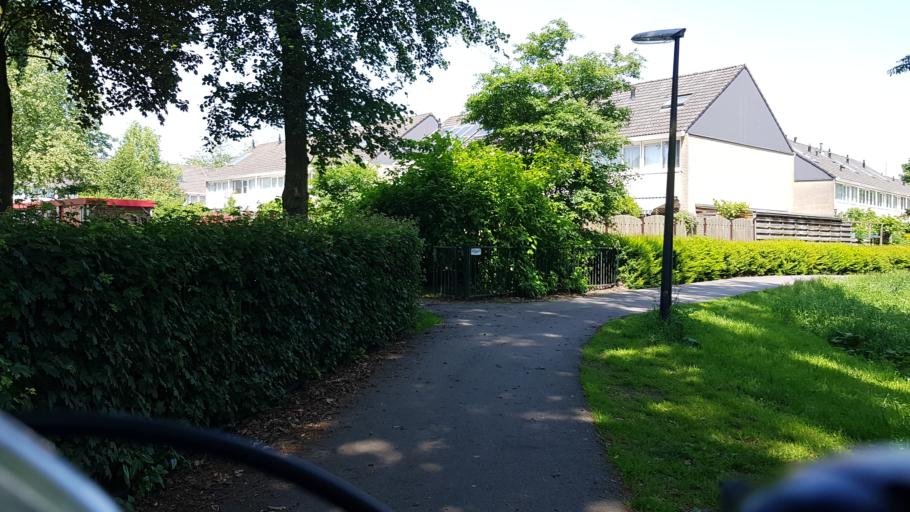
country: NL
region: Gelderland
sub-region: Gemeente Apeldoorn
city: Apeldoorn
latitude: 52.1920
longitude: 5.9959
